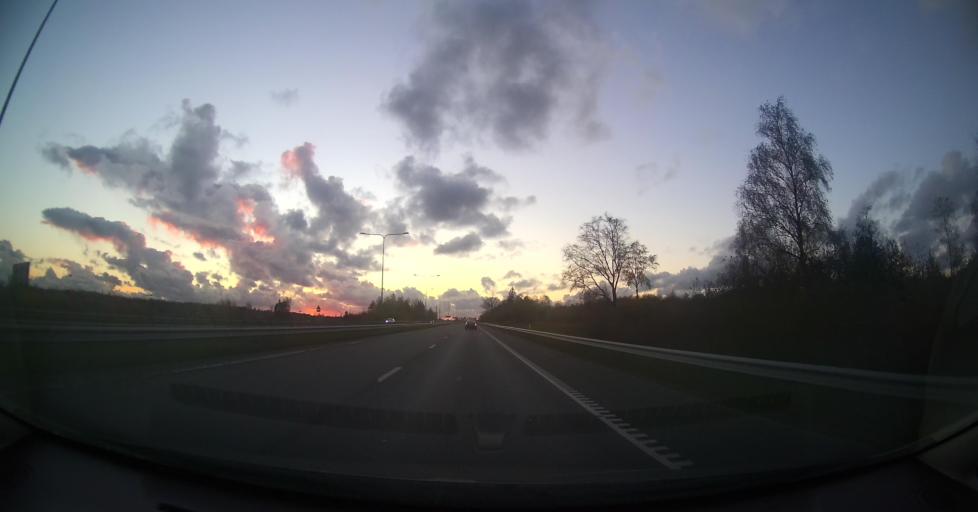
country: EE
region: Harju
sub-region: Maardu linn
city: Maardu
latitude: 59.4503
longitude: 25.0357
